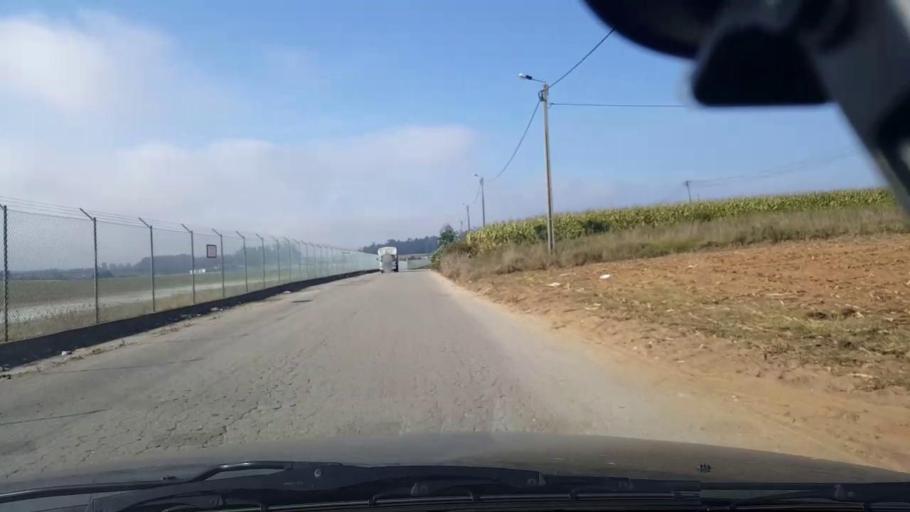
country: PT
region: Porto
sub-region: Matosinhos
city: Lavra
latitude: 41.2635
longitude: -8.6830
